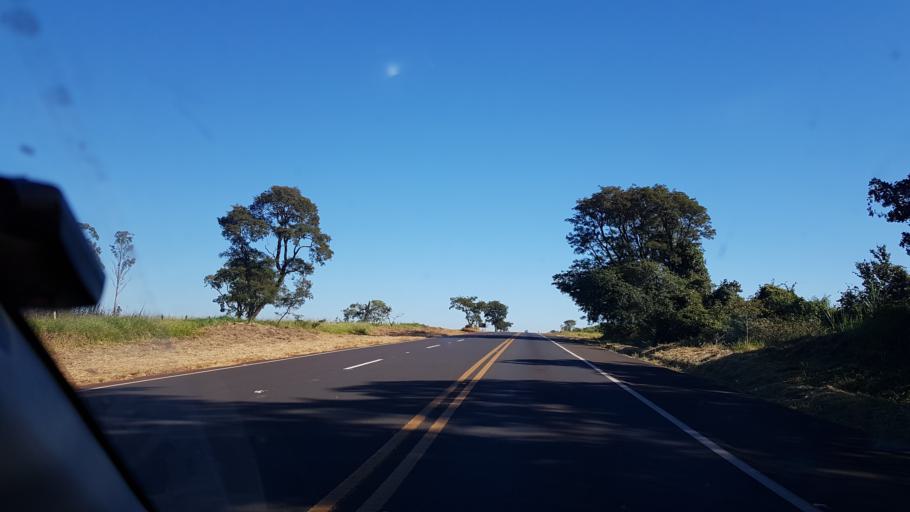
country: BR
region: Sao Paulo
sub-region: Assis
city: Assis
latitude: -22.5773
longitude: -50.5108
